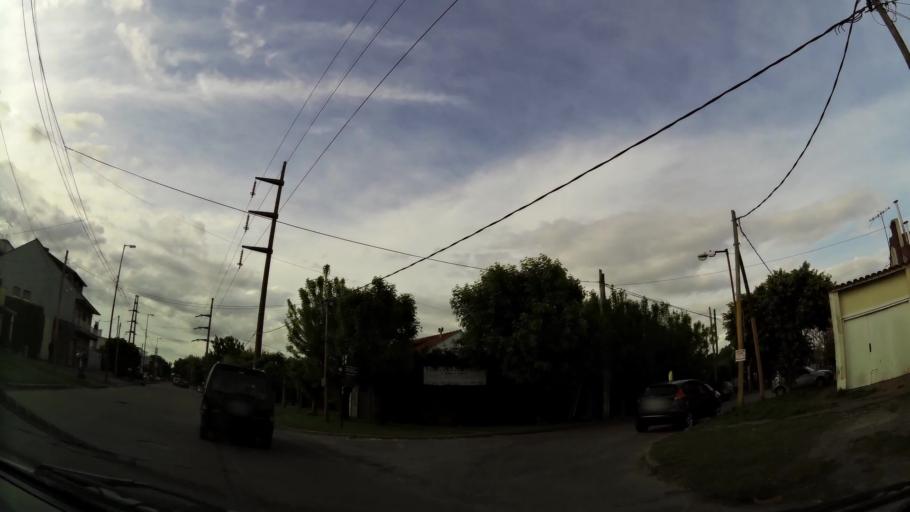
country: AR
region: Buenos Aires
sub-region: Partido de Quilmes
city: Quilmes
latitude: -34.7386
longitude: -58.2705
